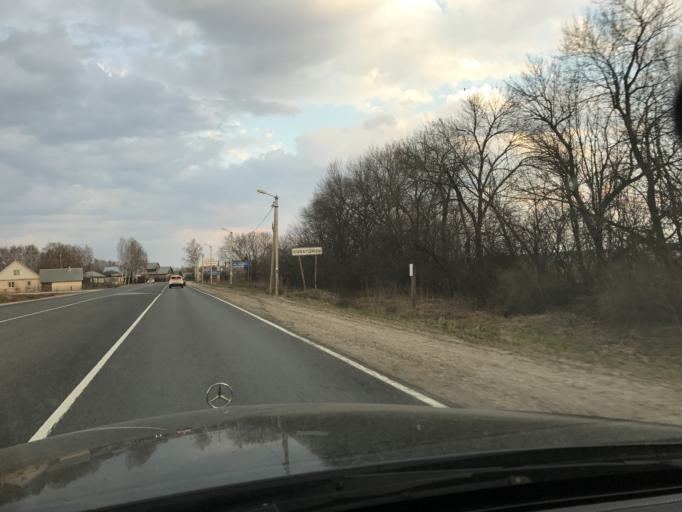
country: RU
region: Vladimir
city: Murom
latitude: 55.6167
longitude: 41.9414
